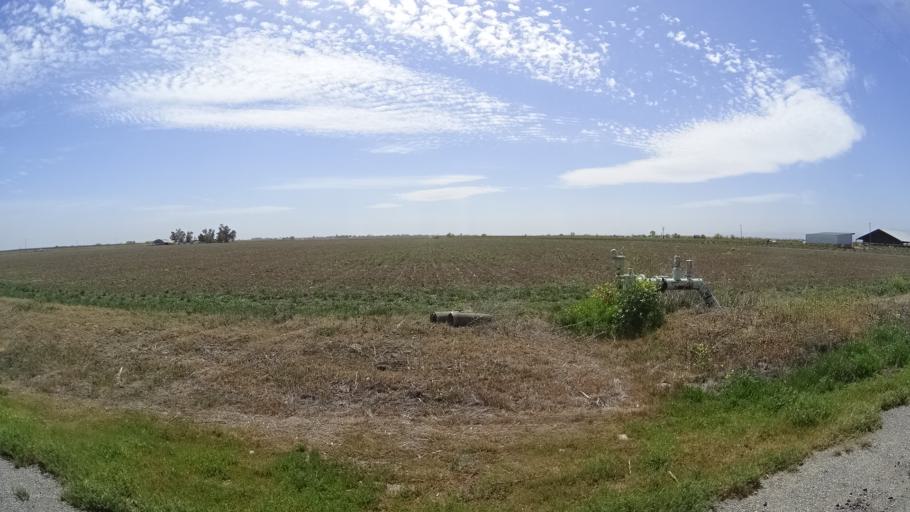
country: US
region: California
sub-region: Glenn County
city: Willows
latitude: 39.5732
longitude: -122.2077
